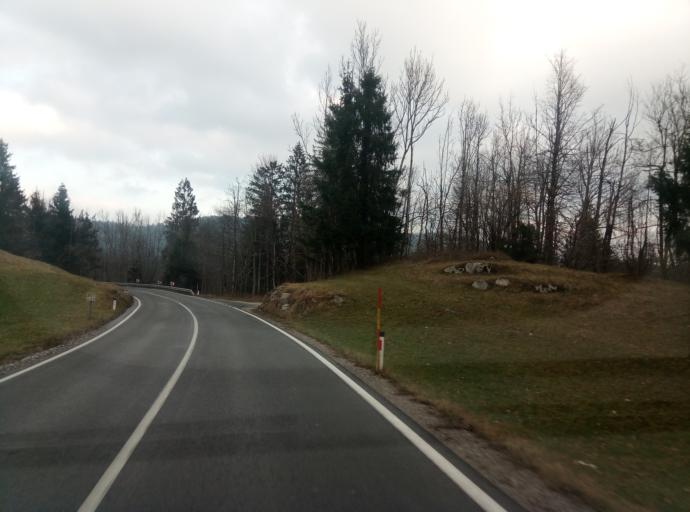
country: SI
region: Idrija
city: Idrija
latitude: 45.9513
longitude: 14.0790
